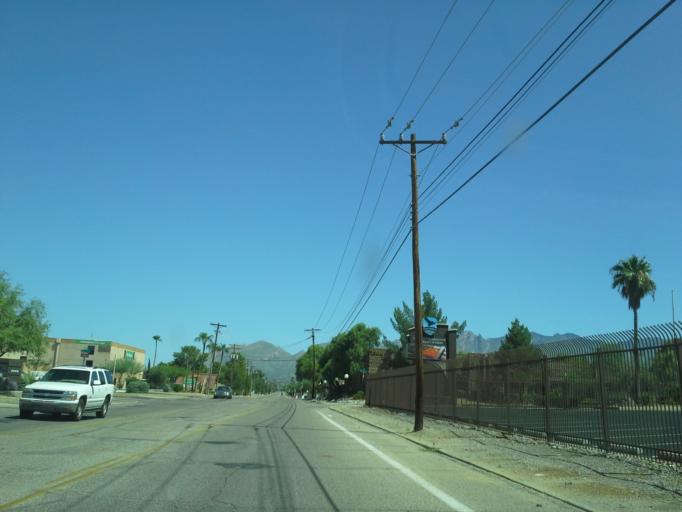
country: US
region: Arizona
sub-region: Pima County
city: Tucson
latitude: 32.2515
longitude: -110.9354
